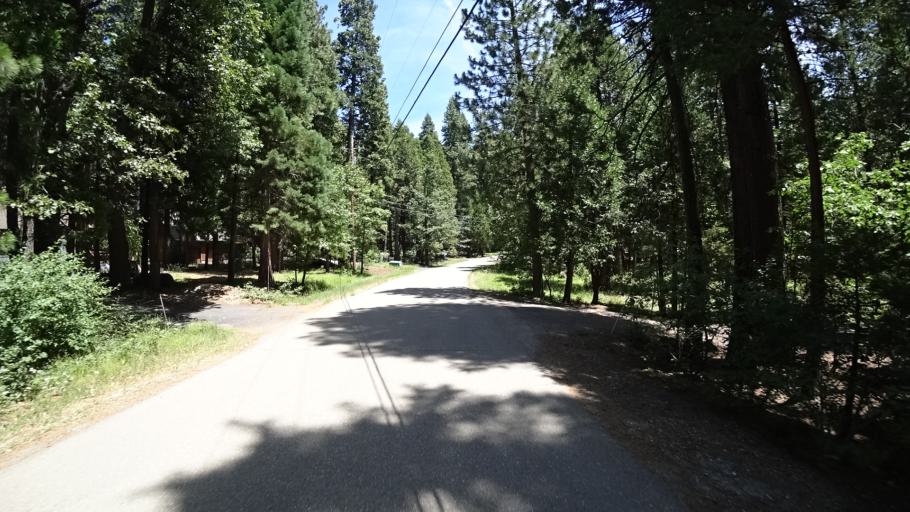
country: US
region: California
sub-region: Calaveras County
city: Arnold
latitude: 38.3013
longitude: -120.2671
